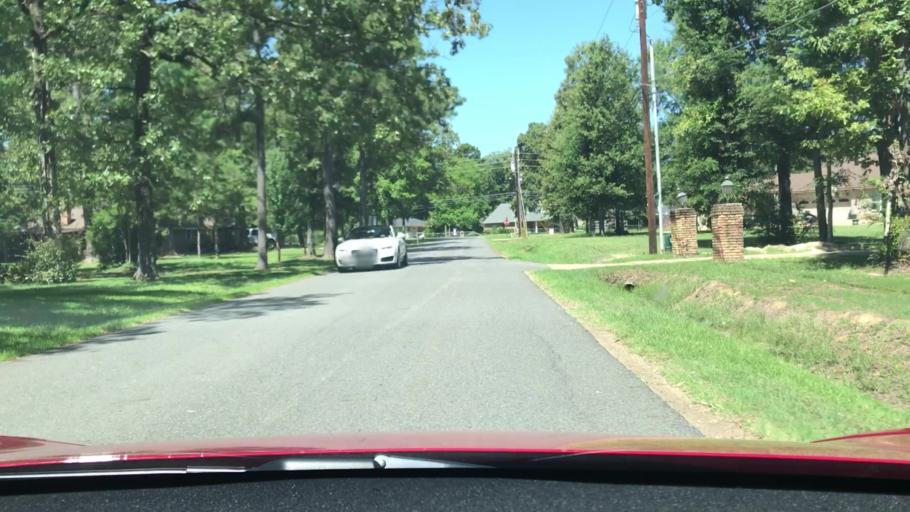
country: US
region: Louisiana
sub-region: De Soto Parish
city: Stonewall
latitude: 32.3449
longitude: -93.7124
